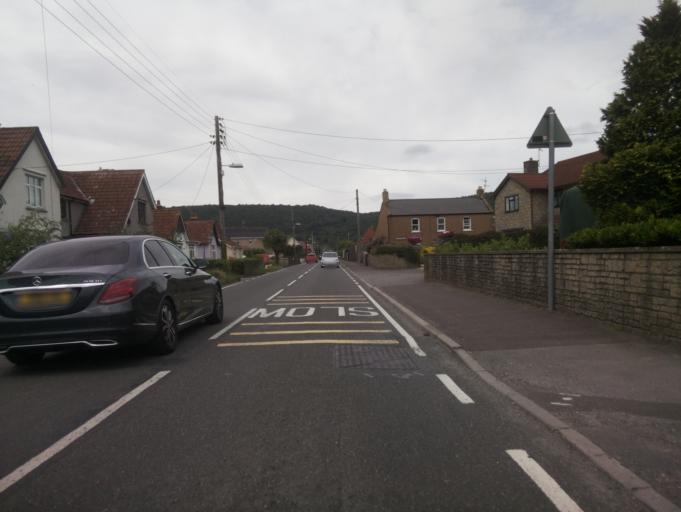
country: GB
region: England
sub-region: Somerset
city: Cheddar
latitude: 51.2789
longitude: -2.7887
